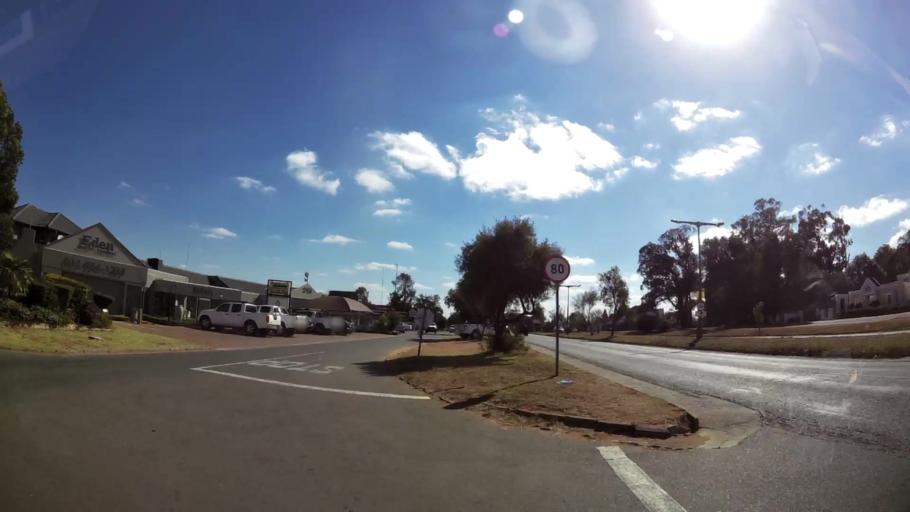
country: ZA
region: Gauteng
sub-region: West Rand District Municipality
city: Krugersdorp
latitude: -26.1071
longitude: 27.8015
